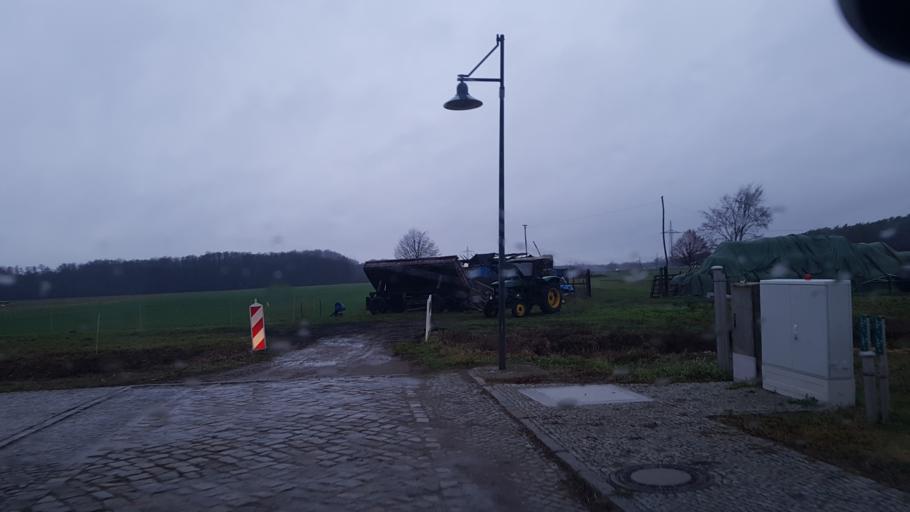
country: DE
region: Brandenburg
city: Ludwigsfelde
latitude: 52.3167
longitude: 13.1925
